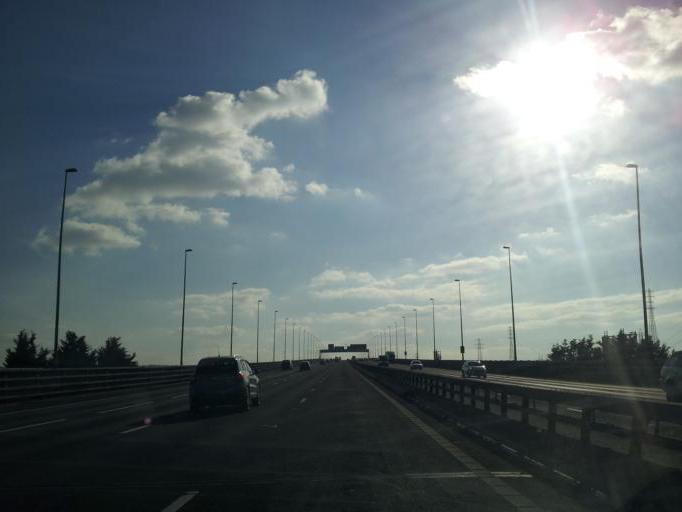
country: GB
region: England
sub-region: North Somerset
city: Easton-in-Gordano
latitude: 51.4949
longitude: -2.6864
